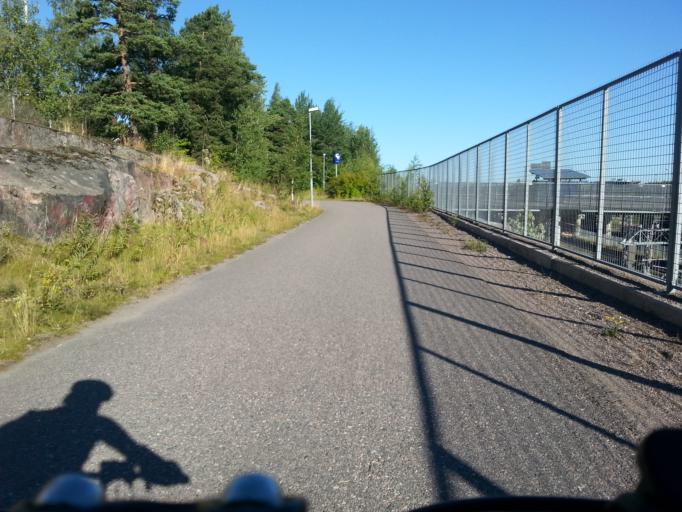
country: FI
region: Uusimaa
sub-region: Helsinki
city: Helsinki
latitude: 60.2062
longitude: 24.9235
